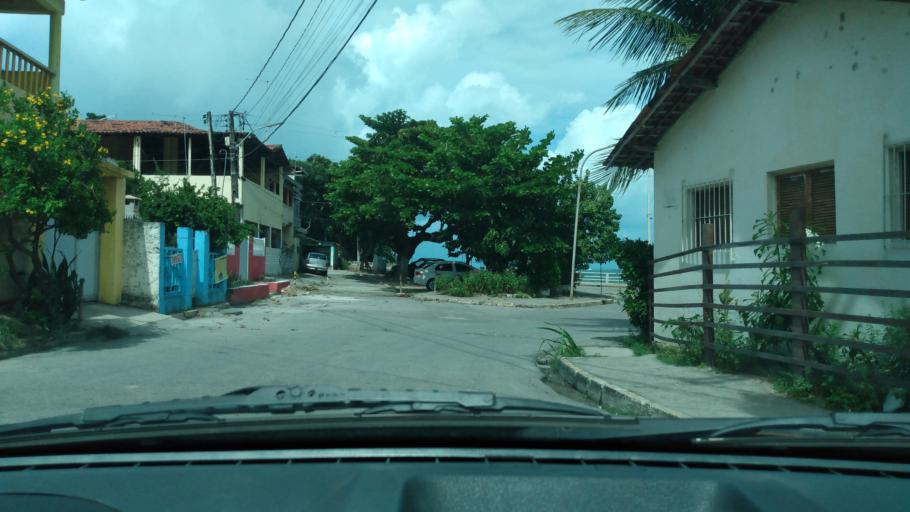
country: BR
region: Pernambuco
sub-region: Cabo De Santo Agostinho
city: Cabo
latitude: -8.3543
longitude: -34.9550
